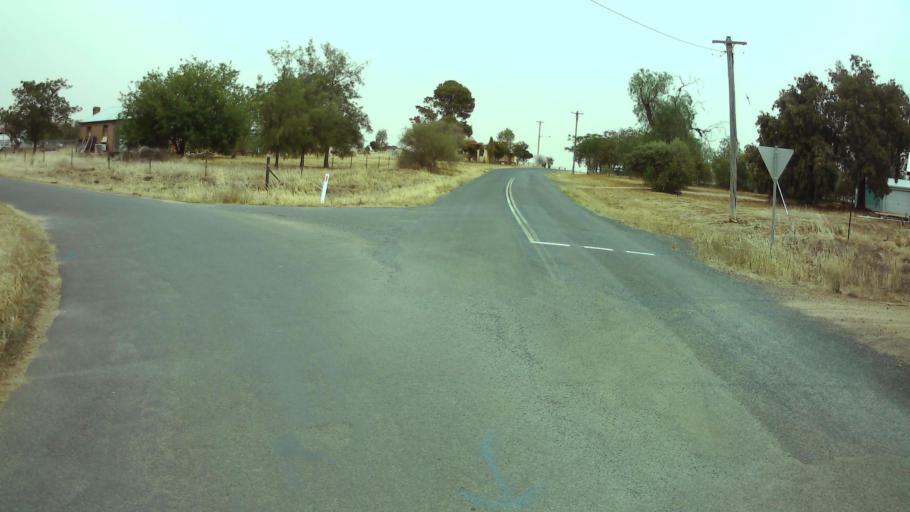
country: AU
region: New South Wales
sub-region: Weddin
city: Grenfell
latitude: -33.9009
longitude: 148.1694
